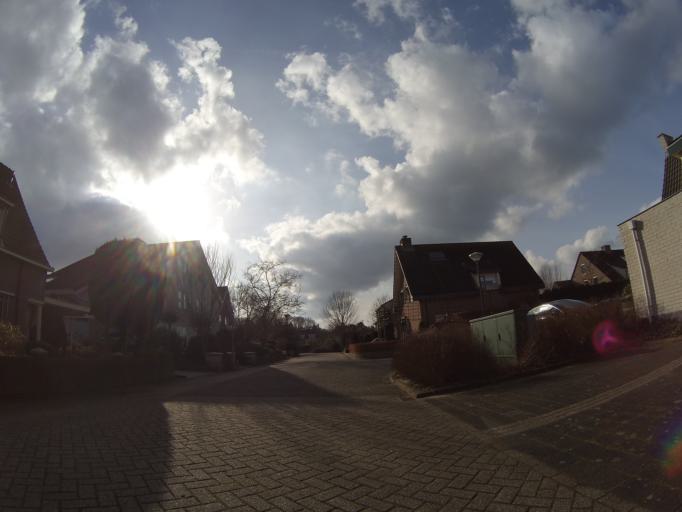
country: NL
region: Utrecht
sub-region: Gemeente Soest
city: Soest
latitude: 52.1635
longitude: 5.2786
